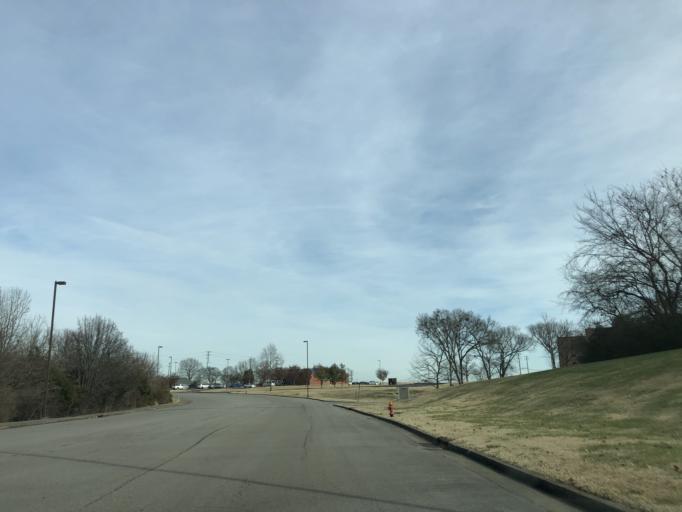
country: US
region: Tennessee
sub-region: Davidson County
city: Nashville
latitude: 36.2156
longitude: -86.7450
